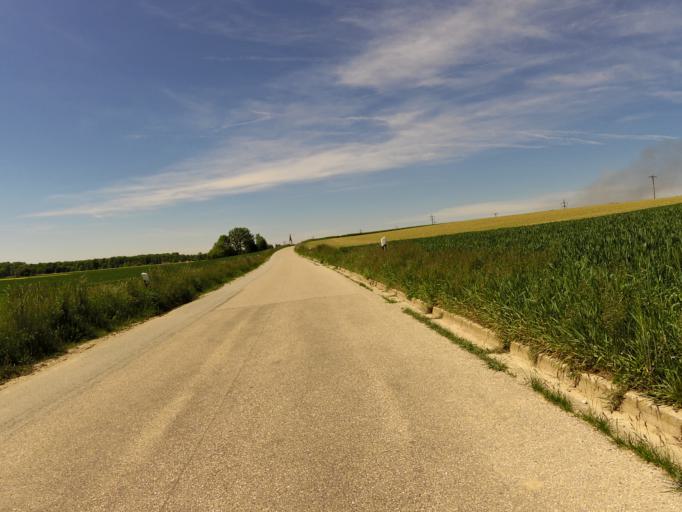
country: DE
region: Bavaria
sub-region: Upper Bavaria
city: Moosburg
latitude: 48.4717
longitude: 11.8958
